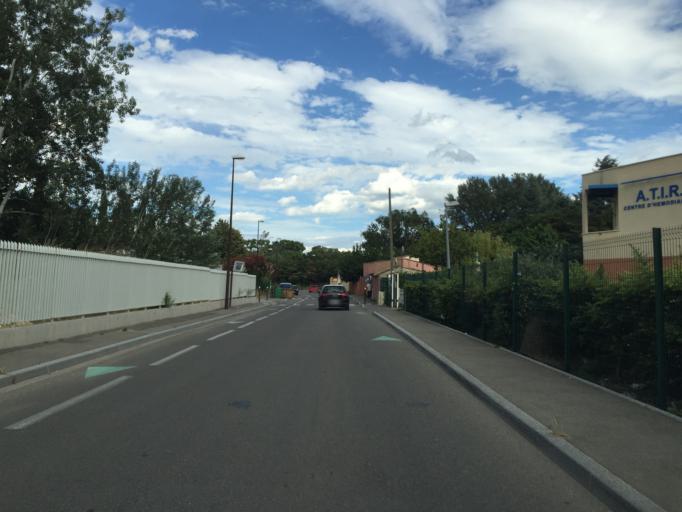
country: FR
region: Provence-Alpes-Cote d'Azur
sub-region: Departement des Bouches-du-Rhone
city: Rognonas
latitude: 43.9227
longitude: 4.8014
